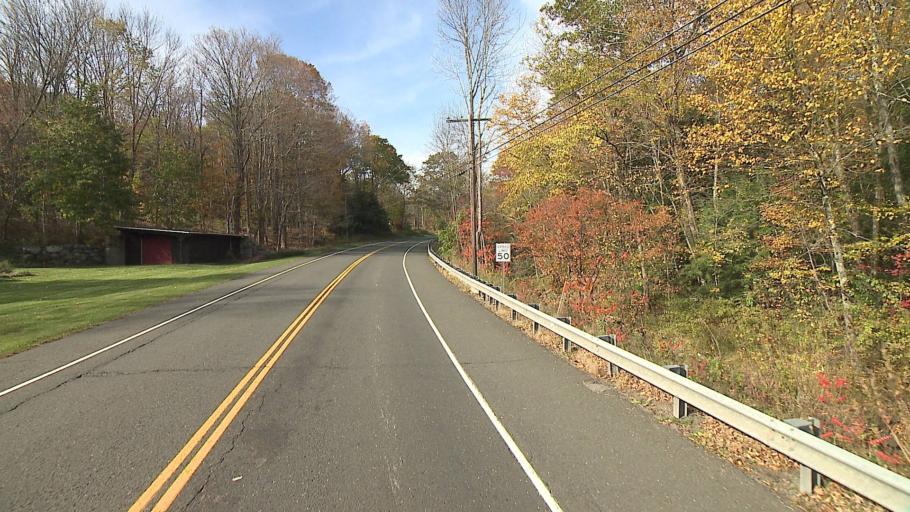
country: US
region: Connecticut
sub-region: Litchfield County
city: Winchester Center
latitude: 41.9449
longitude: -73.1130
